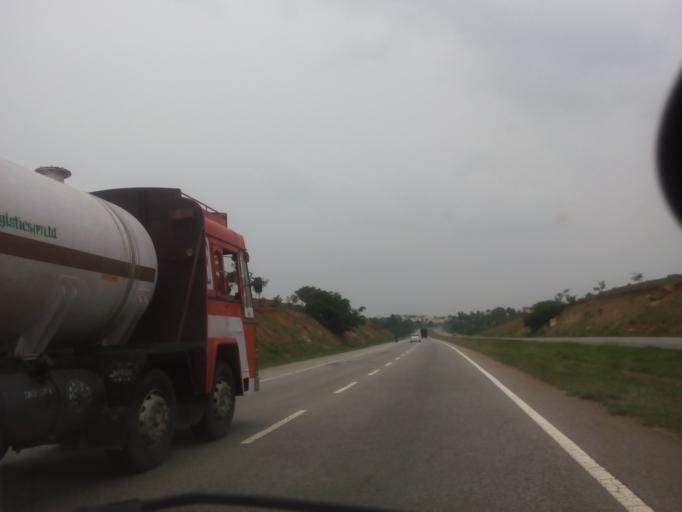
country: IN
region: Karnataka
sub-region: Bangalore Urban
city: Bangalore
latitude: 12.9750
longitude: 77.4712
